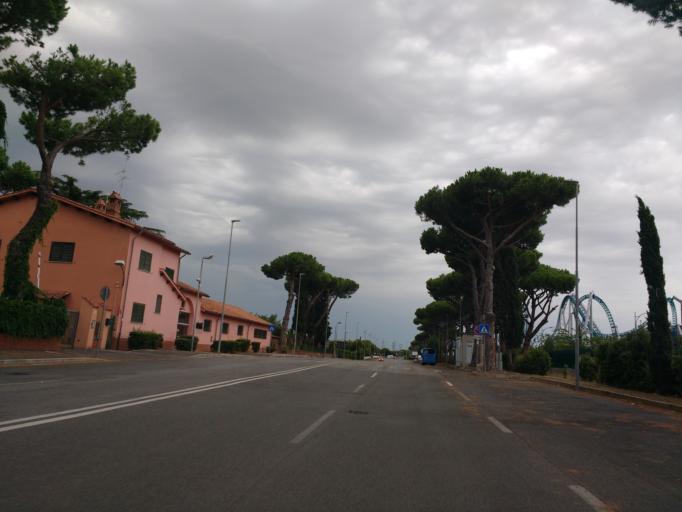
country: IT
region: Latium
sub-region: Citta metropolitana di Roma Capitale
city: Monte Migliore-La Selvotta
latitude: 41.7140
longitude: 12.4481
